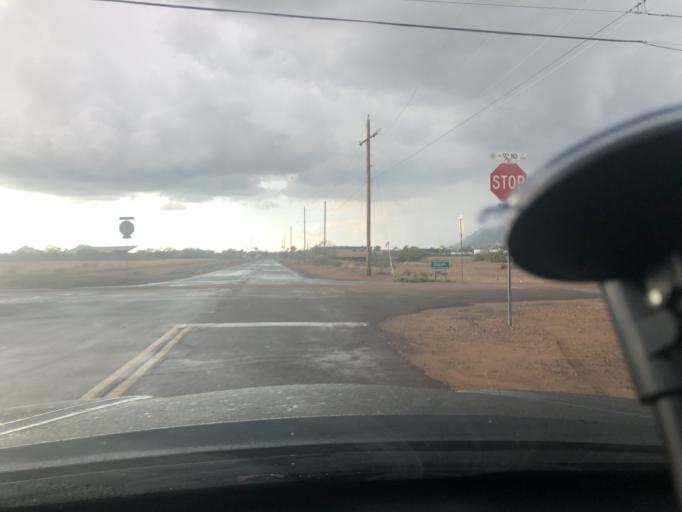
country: US
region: Arizona
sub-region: Maricopa County
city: Scottsdale
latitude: 33.4877
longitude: -111.8824
